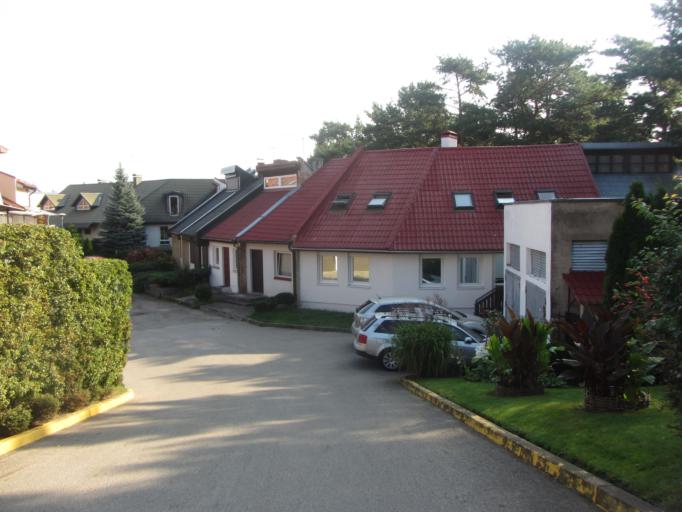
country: LT
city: Nida
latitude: 55.3018
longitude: 21.0015
